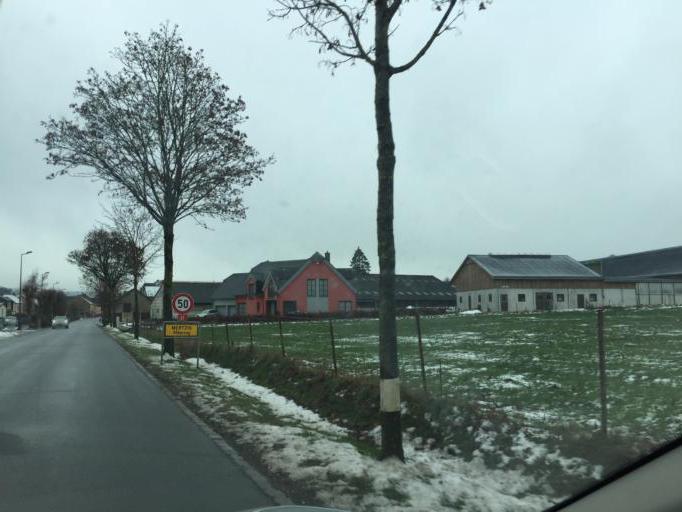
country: LU
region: Diekirch
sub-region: Canton de Diekirch
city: Mertzig
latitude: 49.8366
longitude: 6.0116
